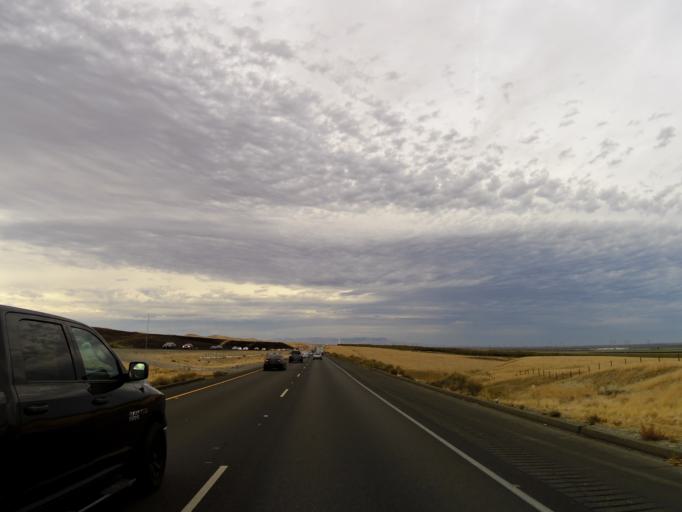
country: US
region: California
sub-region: Kings County
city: Kettleman City
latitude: 36.0317
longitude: -120.0244
